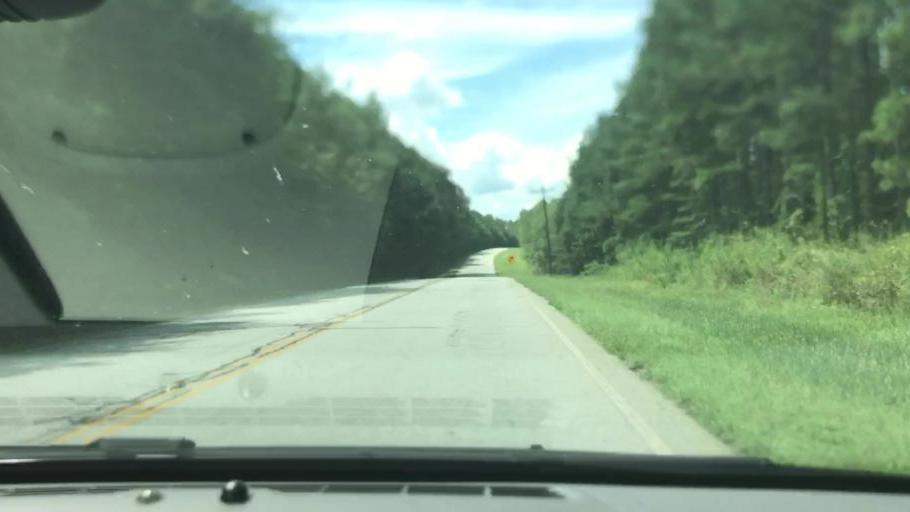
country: US
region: Georgia
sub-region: Stewart County
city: Lumpkin
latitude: 32.1389
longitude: -84.9423
